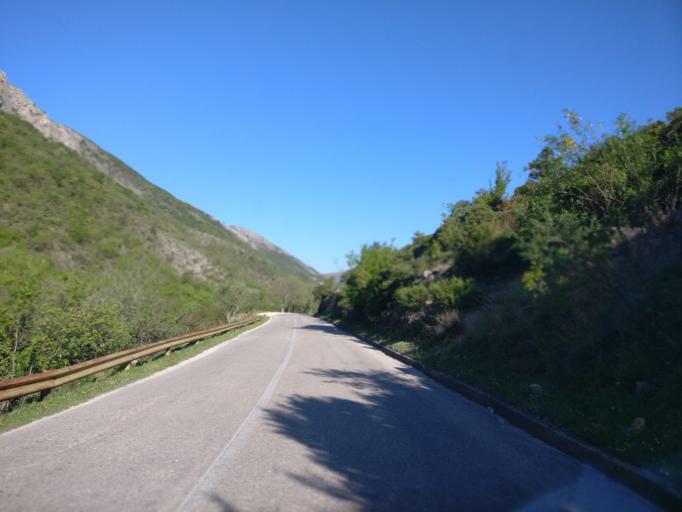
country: BA
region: Federation of Bosnia and Herzegovina
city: Stolac
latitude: 43.0811
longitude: 18.0122
